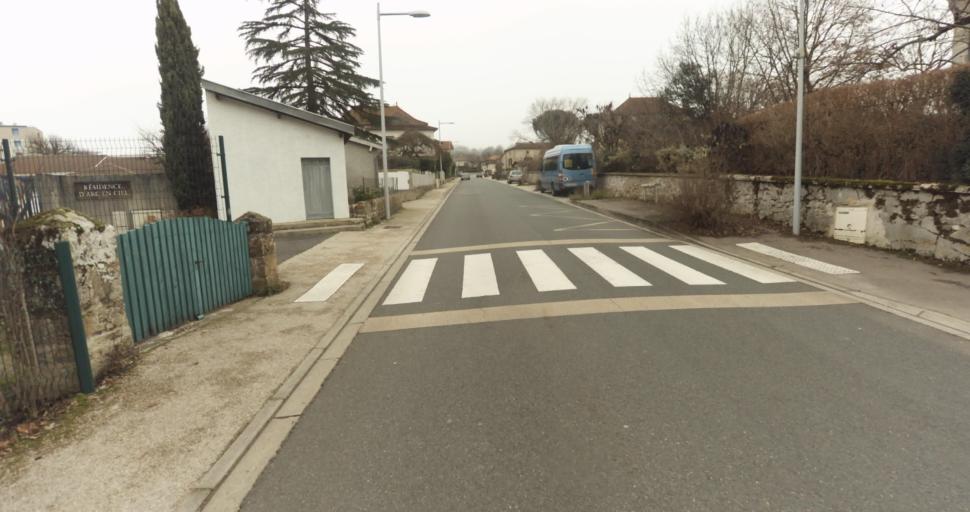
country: FR
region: Midi-Pyrenees
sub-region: Departement du Lot
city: Figeac
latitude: 44.6126
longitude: 2.0377
